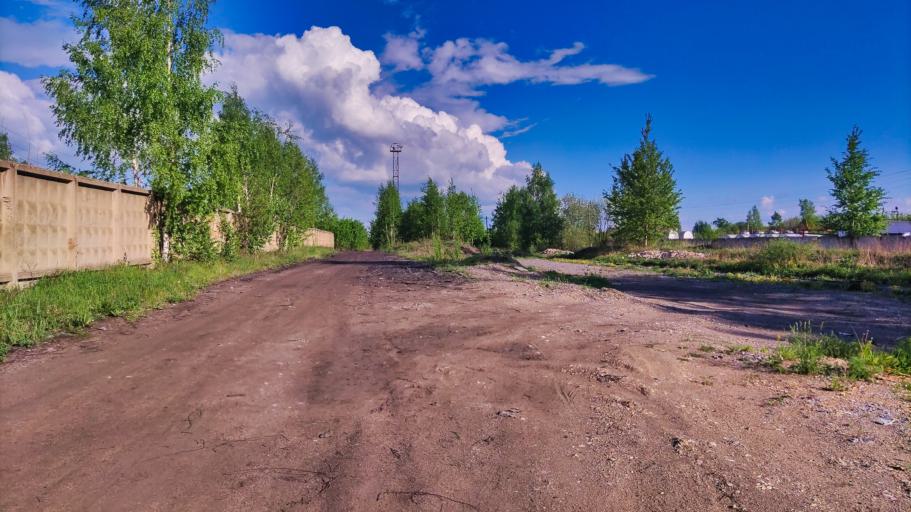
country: RU
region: Tverskaya
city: Rzhev
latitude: 56.2406
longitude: 34.3405
